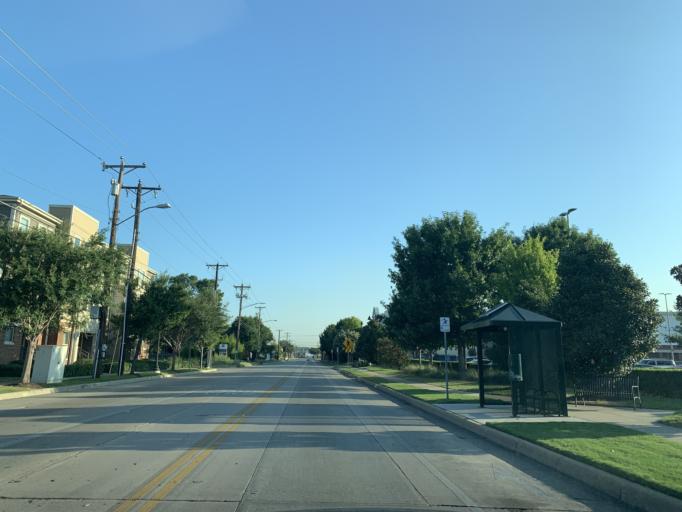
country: US
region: Texas
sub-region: Tarrant County
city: Fort Worth
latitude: 32.7546
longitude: -97.3546
